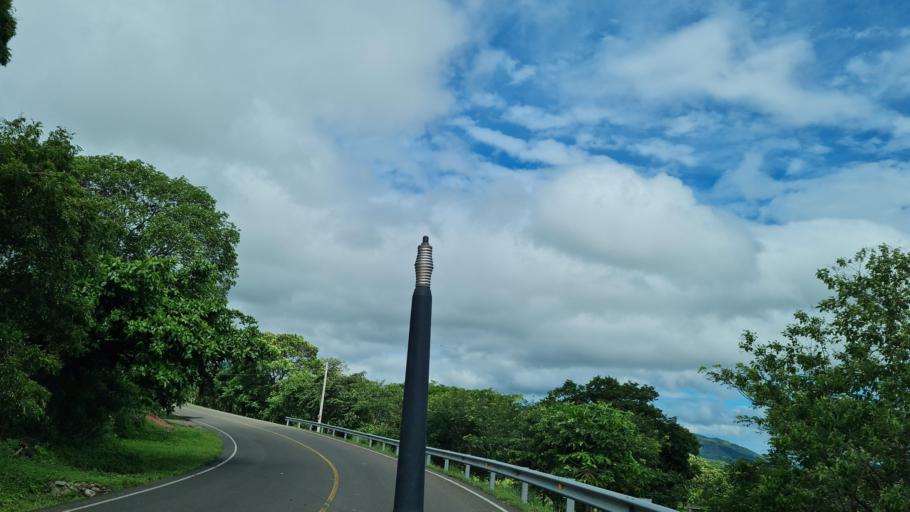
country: NI
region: Boaco
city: San Jose de los Remates
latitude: 12.6115
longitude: -85.8933
